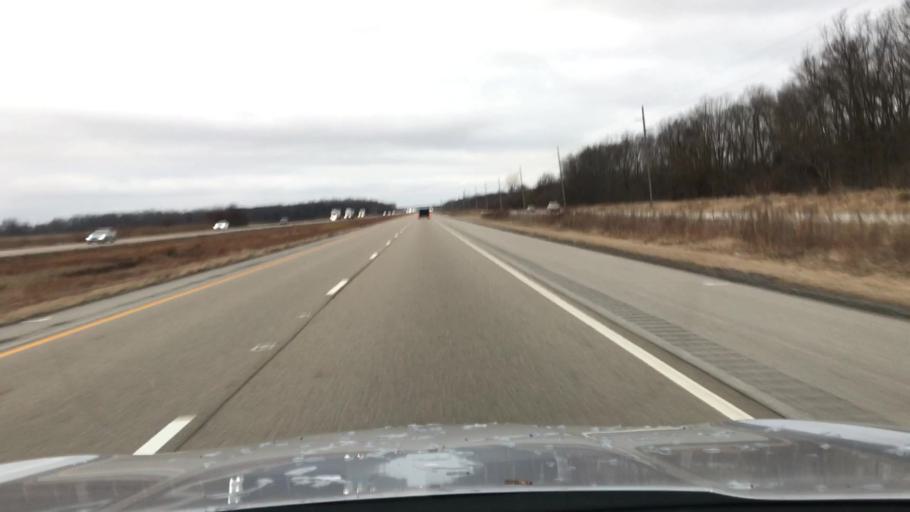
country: US
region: Illinois
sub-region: Logan County
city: Atlanta
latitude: 40.2325
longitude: -89.2646
